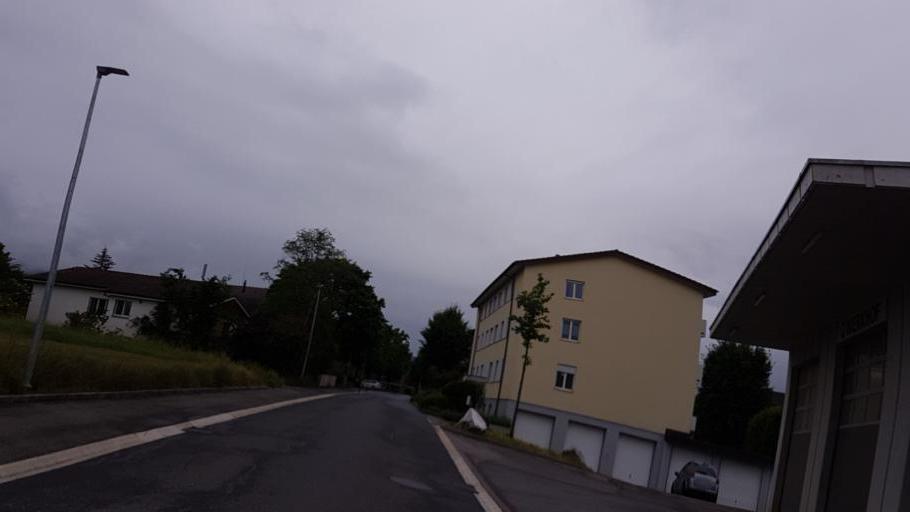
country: CH
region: Bern
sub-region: Bern-Mittelland District
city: Niederwichtrach
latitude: 46.8444
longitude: 7.5695
